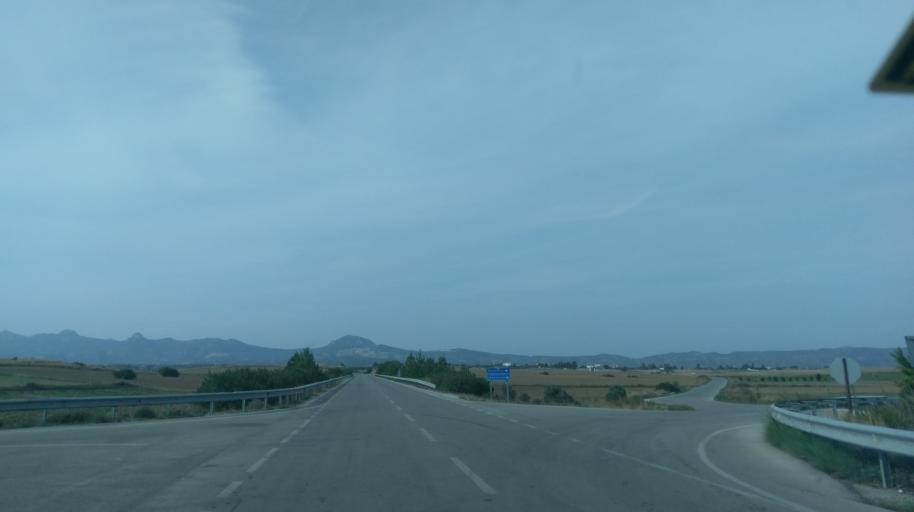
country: CY
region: Ammochostos
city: Leonarisso
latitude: 35.3800
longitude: 34.0218
